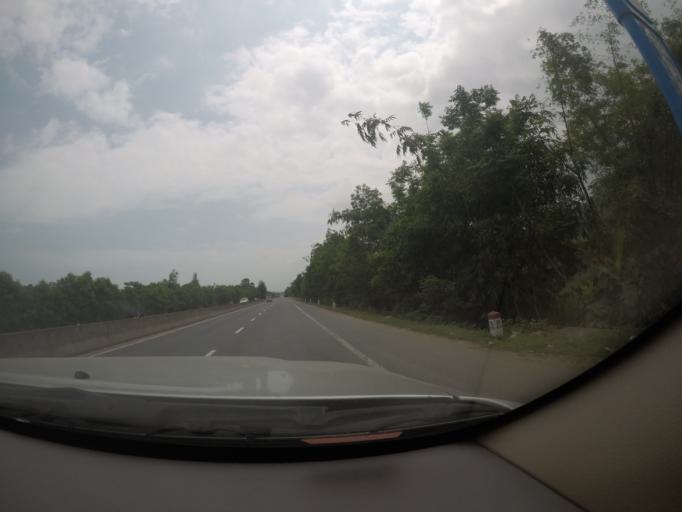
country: VN
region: Thua Thien-Hue
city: Phu Loc
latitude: 16.2888
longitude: 107.8213
